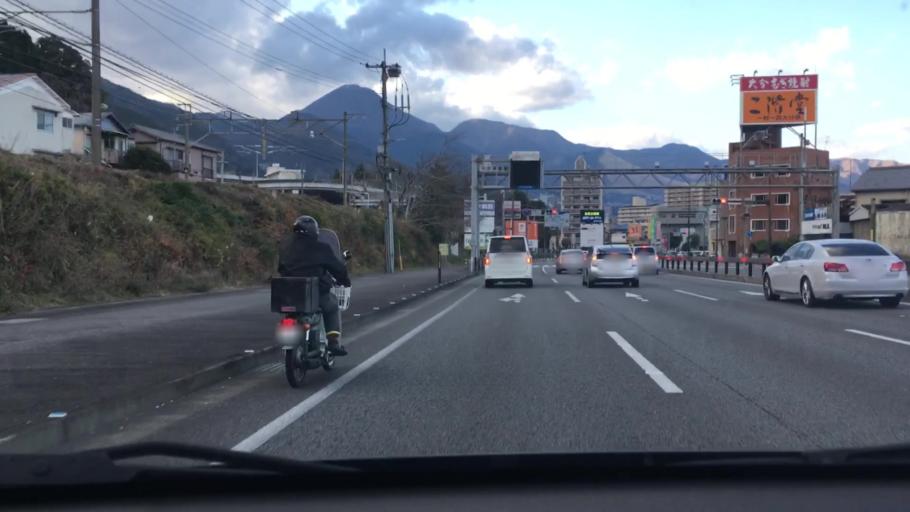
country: JP
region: Oita
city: Beppu
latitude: 33.2671
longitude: 131.5129
